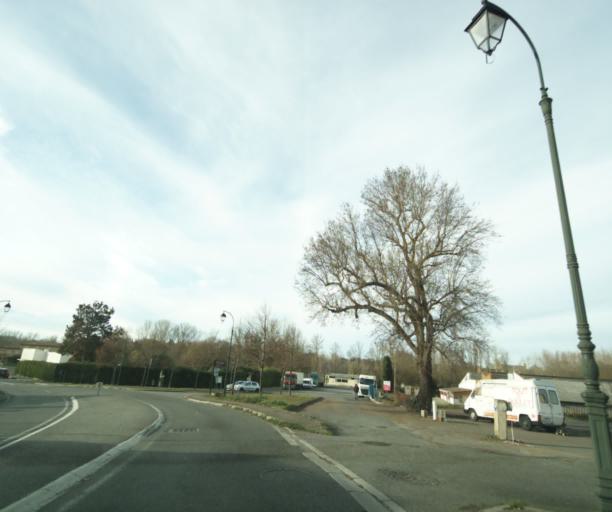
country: FR
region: Midi-Pyrenees
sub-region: Departement du Gers
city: Gimont
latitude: 43.6296
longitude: 0.8736
